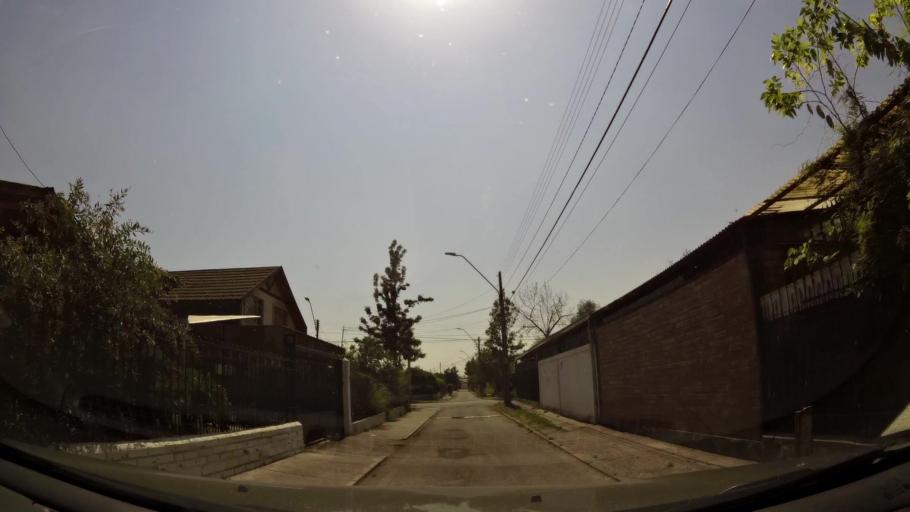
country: CL
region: Santiago Metropolitan
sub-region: Provincia de Maipo
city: San Bernardo
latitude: -33.5824
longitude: -70.7120
